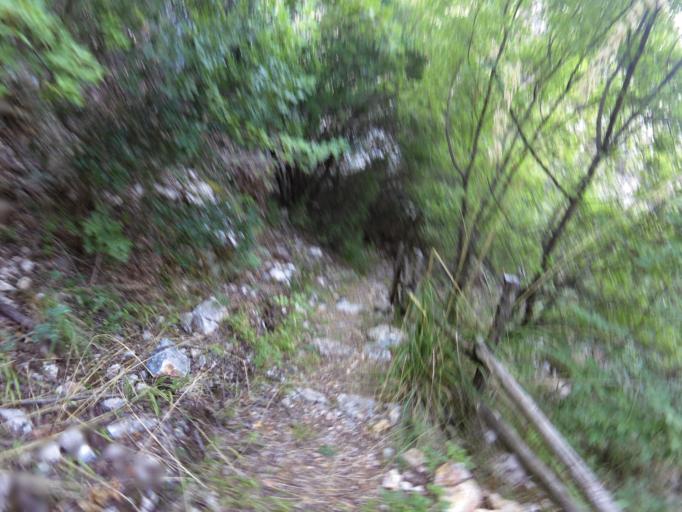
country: IT
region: Calabria
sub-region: Provincia di Reggio Calabria
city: Pazzano
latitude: 38.4719
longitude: 16.4505
